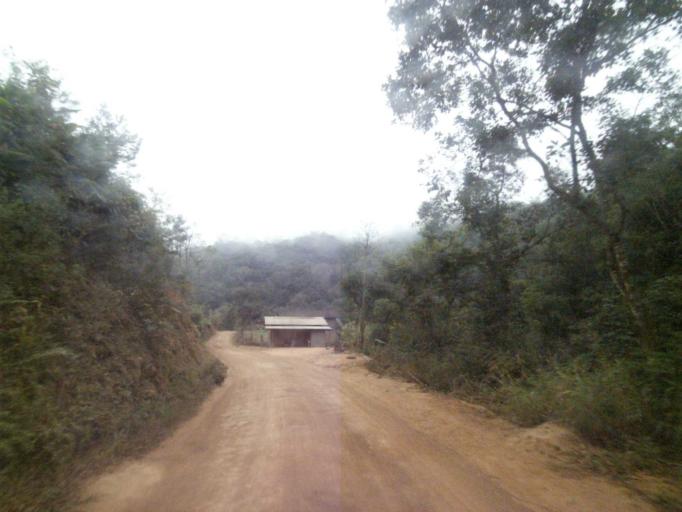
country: BR
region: Santa Catarina
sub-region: Anitapolis
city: Anitapolis
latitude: -27.8954
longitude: -49.1295
